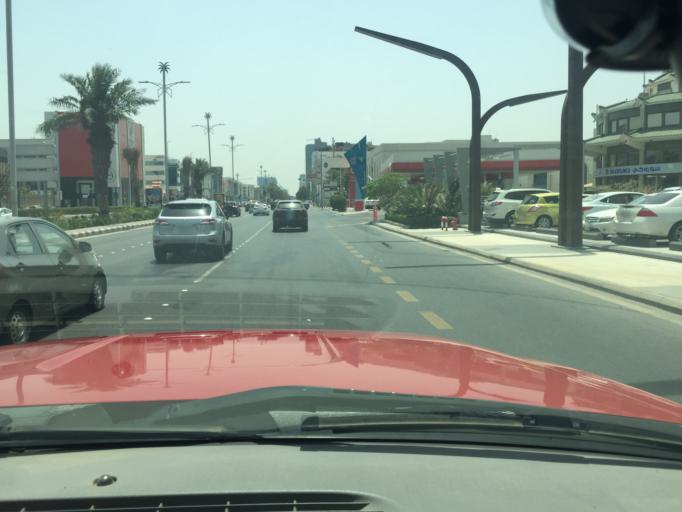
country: SA
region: Makkah
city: Jeddah
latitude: 21.5498
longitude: 39.1534
